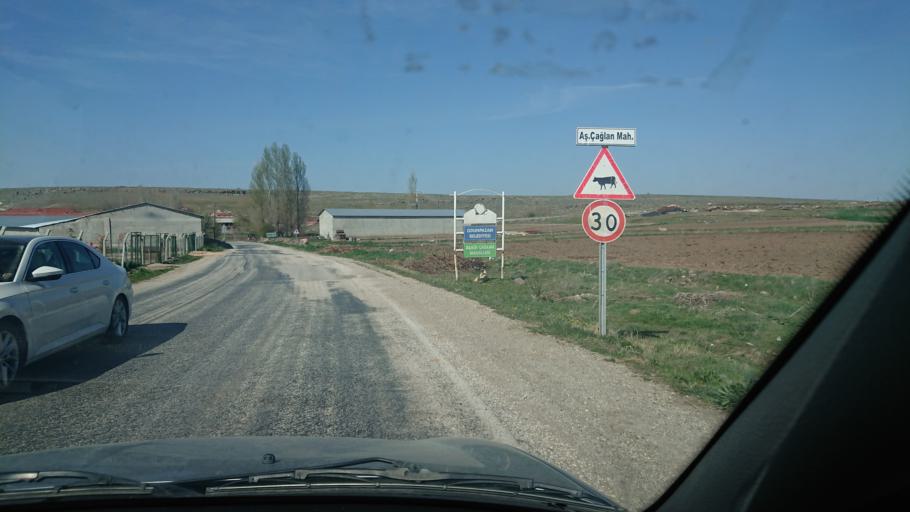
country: TR
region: Eskisehir
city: Eskisehir
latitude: 39.6763
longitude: 30.4846
